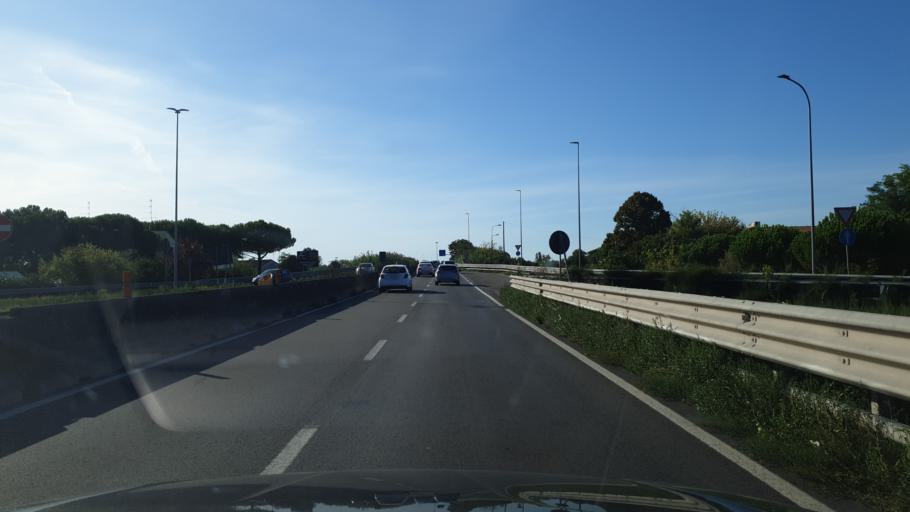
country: IT
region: Emilia-Romagna
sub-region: Provincia di Ravenna
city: Madonna Dell'Albero
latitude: 44.3825
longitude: 12.2007
